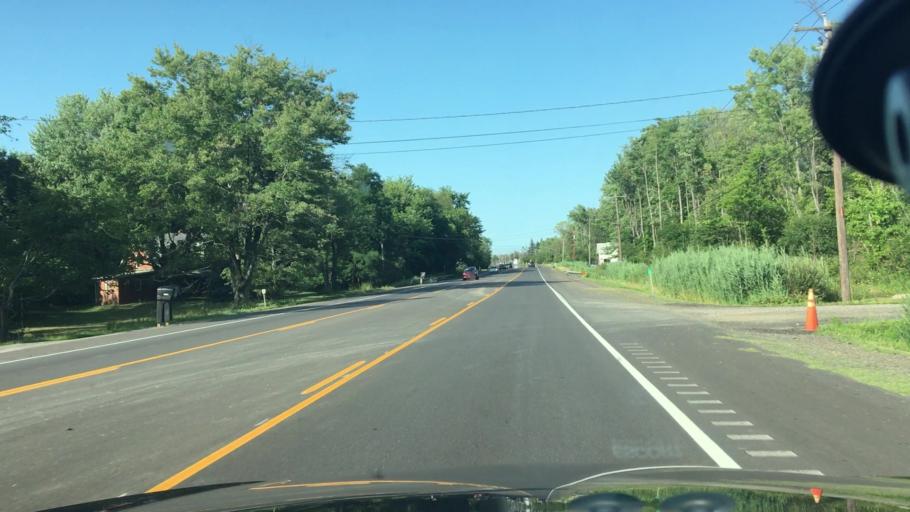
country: US
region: New York
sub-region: Erie County
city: Wanakah
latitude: 42.7221
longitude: -78.8974
